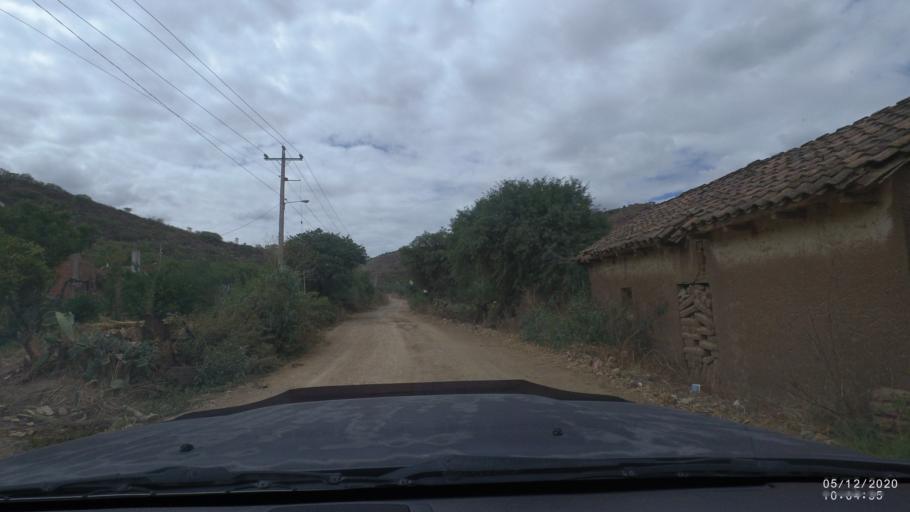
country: BO
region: Cochabamba
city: Sipe Sipe
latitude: -17.4641
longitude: -66.2862
